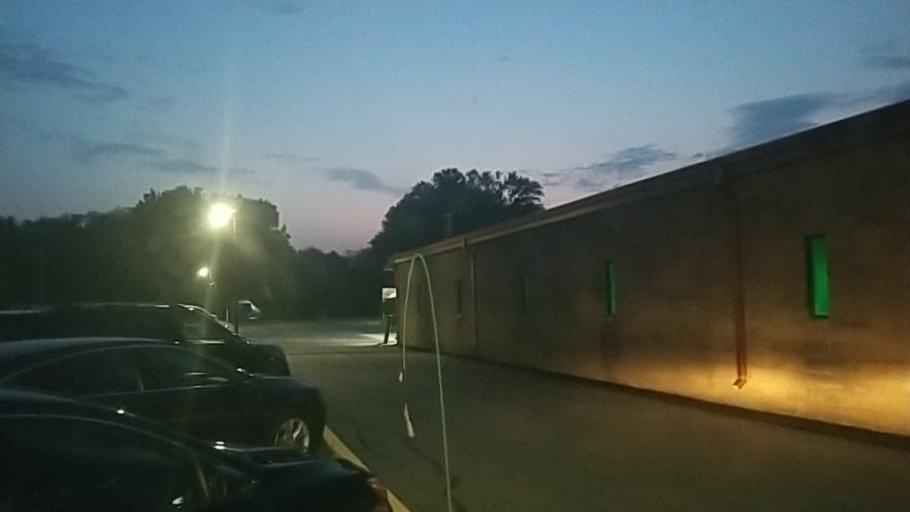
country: US
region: New York
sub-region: Fulton County
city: Johnstown
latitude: 43.0190
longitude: -74.3621
